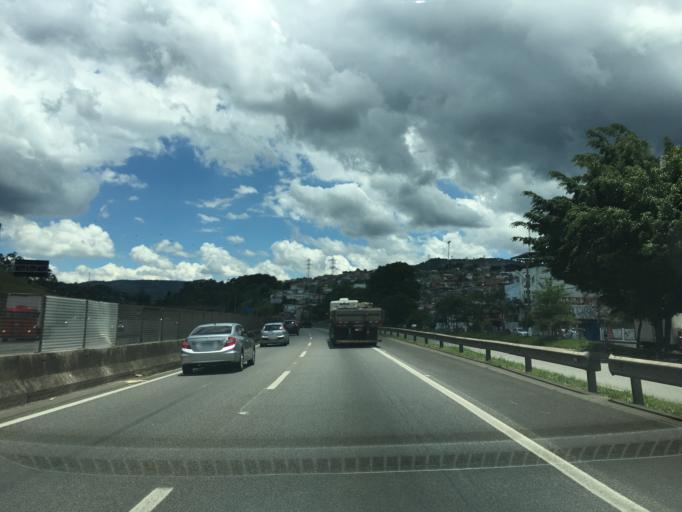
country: BR
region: Sao Paulo
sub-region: Mairipora
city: Mairipora
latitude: -23.3197
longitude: -46.5826
